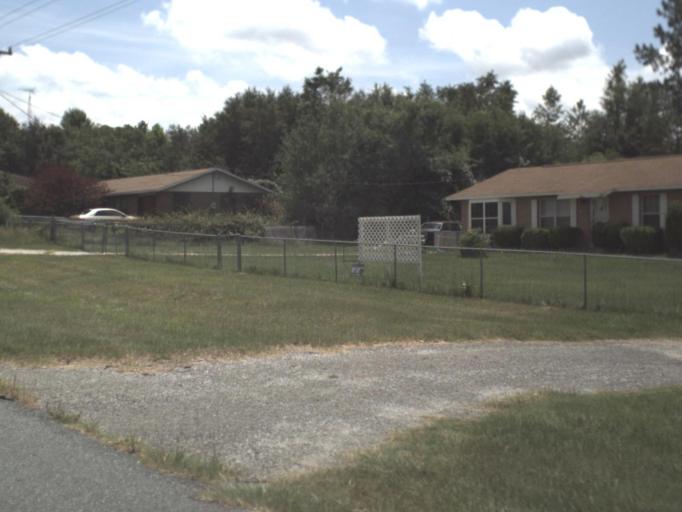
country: US
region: Florida
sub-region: Alachua County
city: High Springs
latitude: 30.0040
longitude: -82.5796
